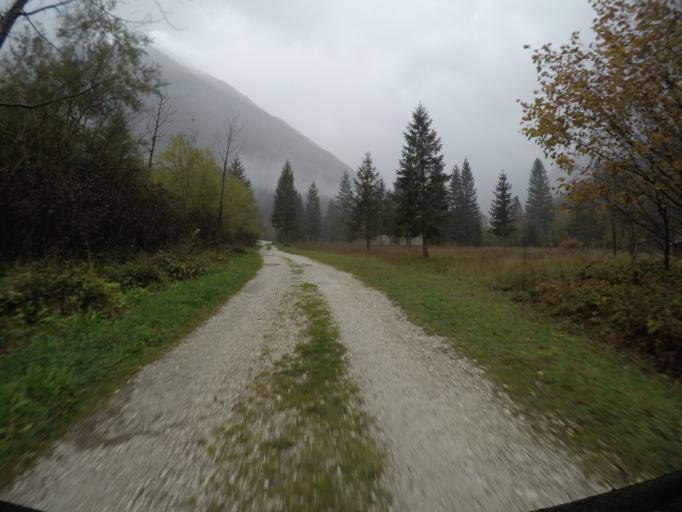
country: SI
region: Bovec
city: Bovec
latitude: 46.3301
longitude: 13.6419
